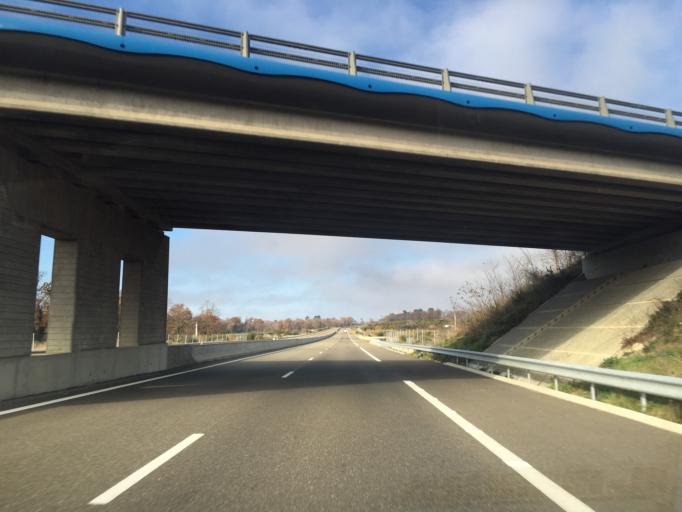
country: FR
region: Aquitaine
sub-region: Departement des Landes
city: Villeneuve-de-Marsan
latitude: 43.7941
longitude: -0.2880
